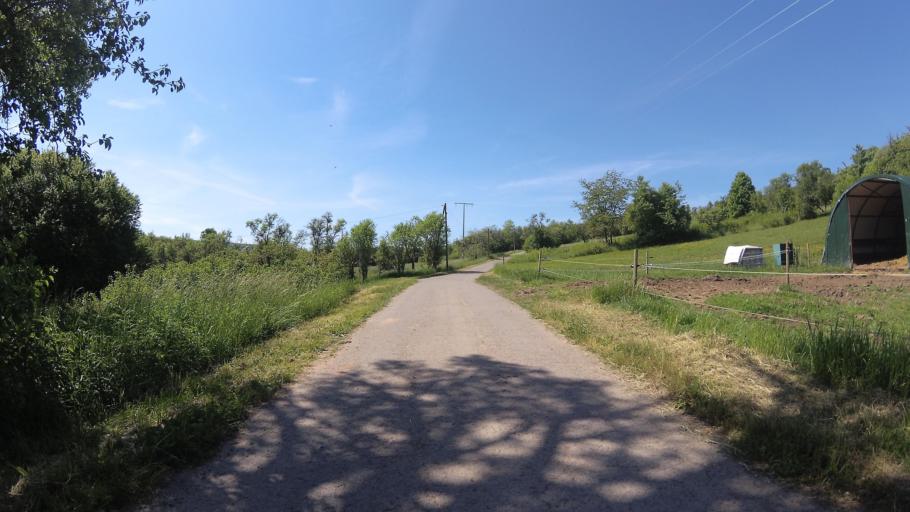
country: DE
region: Saarland
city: Gersheim
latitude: 49.1829
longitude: 7.1606
